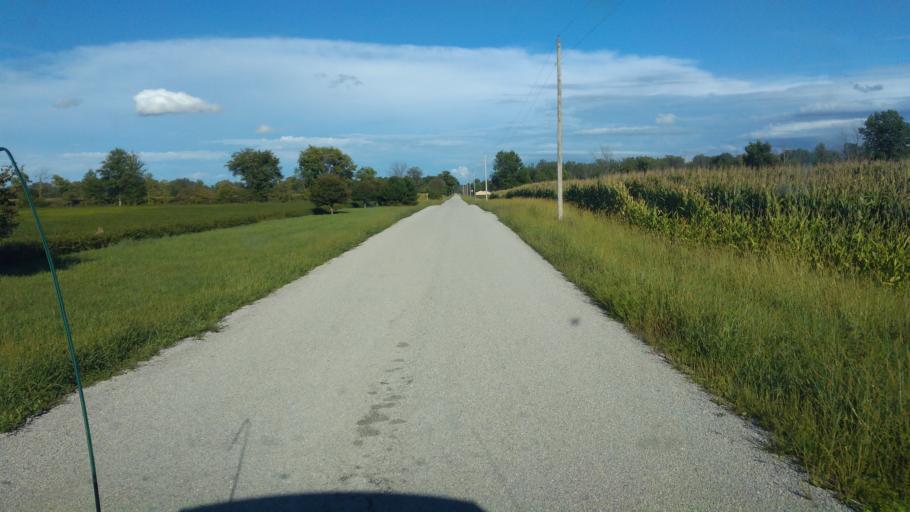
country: US
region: Ohio
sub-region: Hardin County
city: Forest
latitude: 40.7530
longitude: -83.5977
